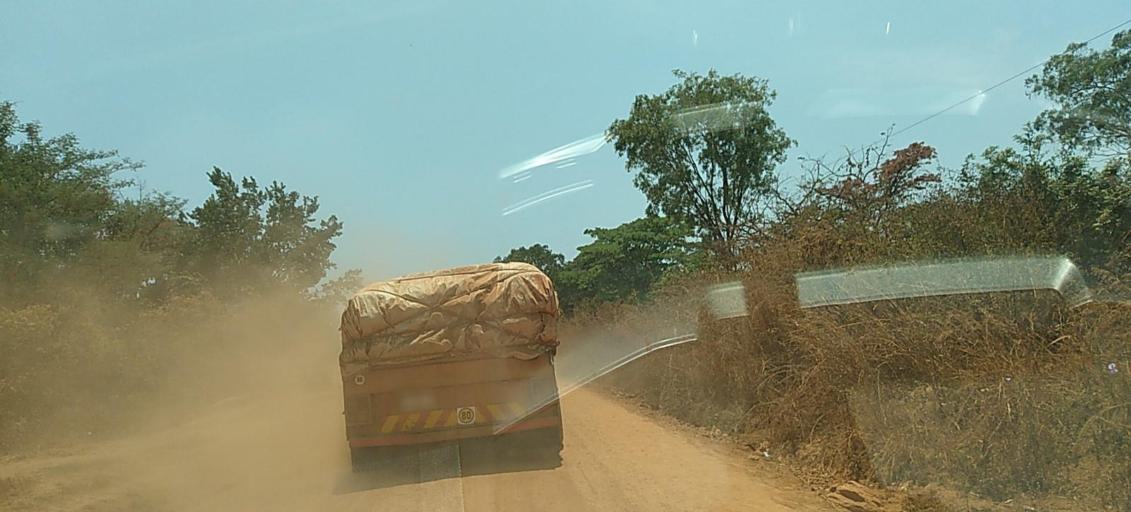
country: CD
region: Katanga
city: Kipushi
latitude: -11.8586
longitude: 27.1185
